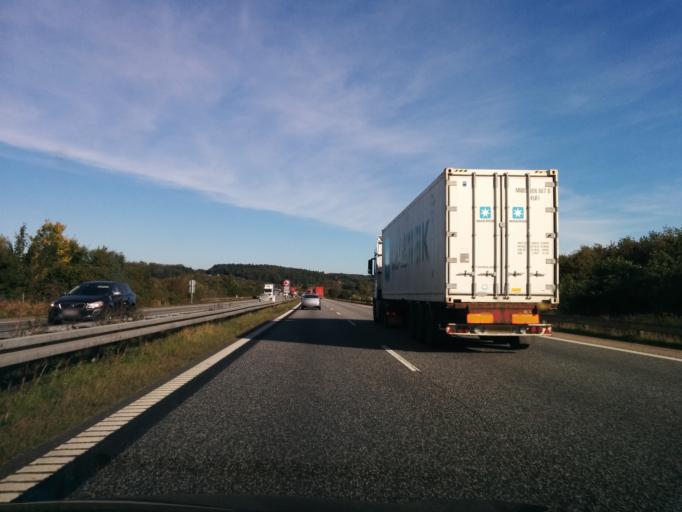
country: DK
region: Central Jutland
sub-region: Horsens Kommune
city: Horsens
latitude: 55.8883
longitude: 9.7973
